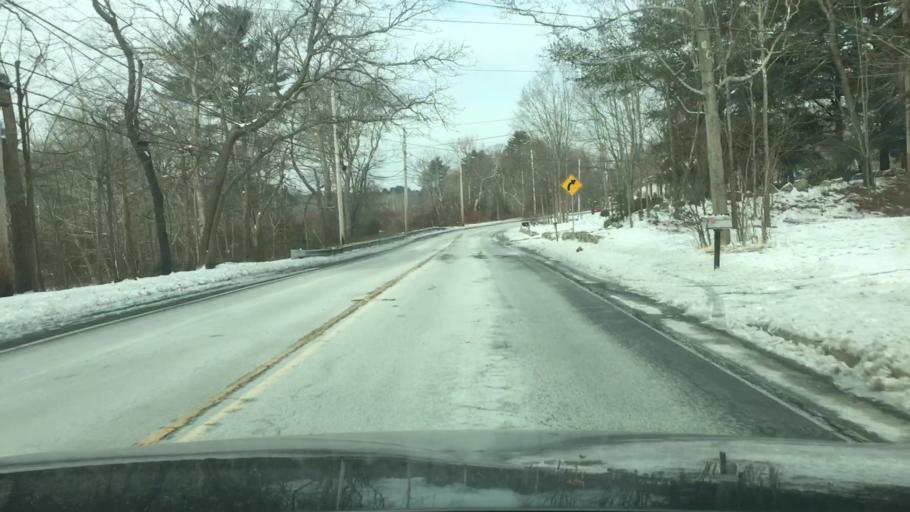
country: US
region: Massachusetts
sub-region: Middlesex County
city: North Reading
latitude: 42.5734
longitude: -71.0531
